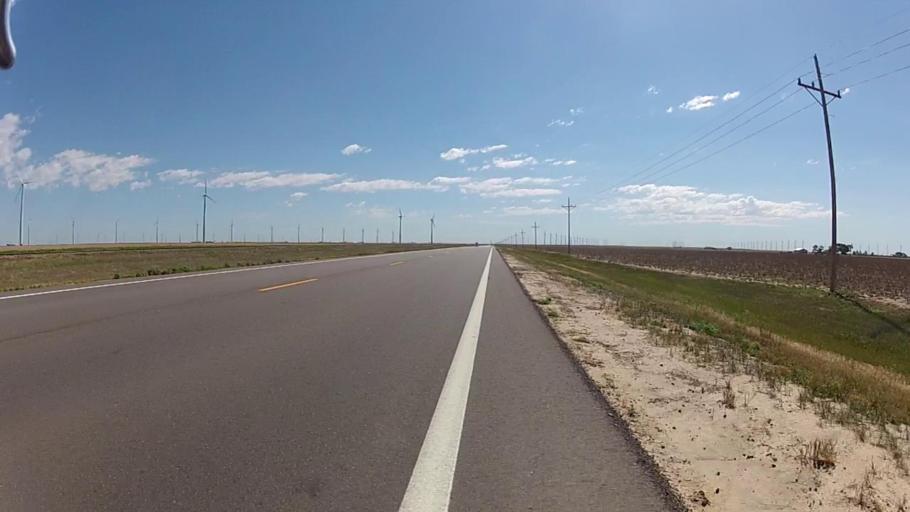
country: US
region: Kansas
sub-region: Gray County
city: Cimarron
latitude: 37.6084
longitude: -100.4103
